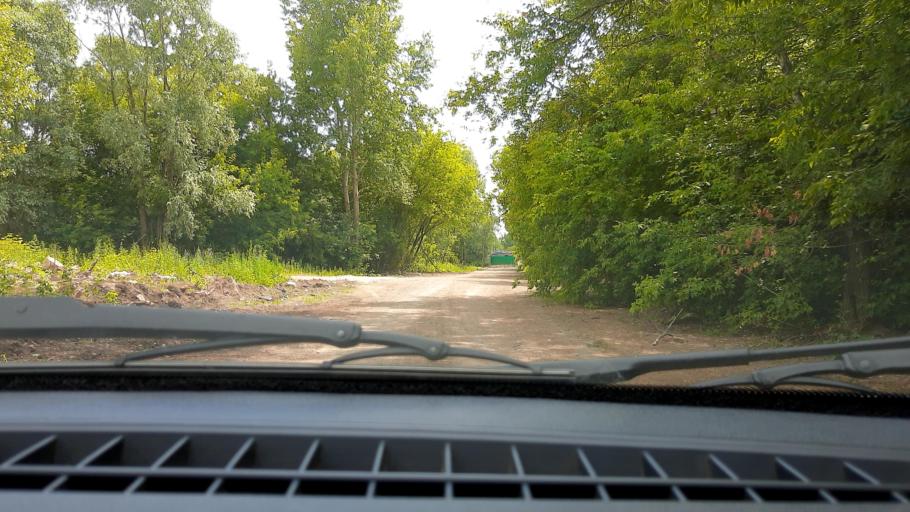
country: RU
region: Bashkortostan
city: Mikhaylovka
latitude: 54.7745
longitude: 55.9105
